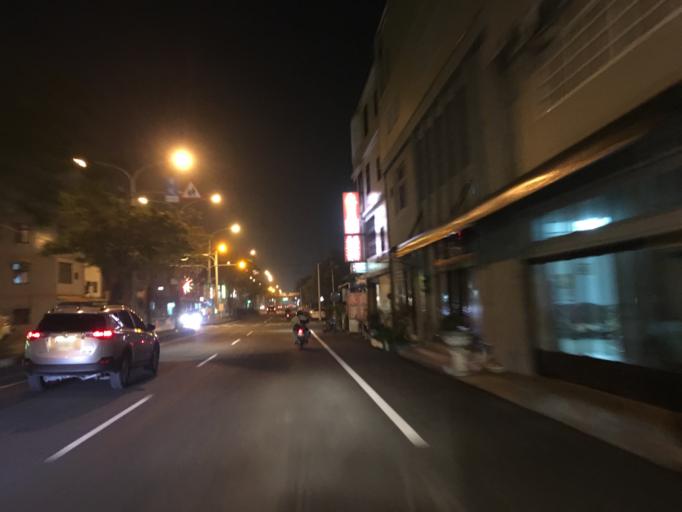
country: TW
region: Taiwan
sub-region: Miaoli
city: Miaoli
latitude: 24.6817
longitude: 120.8850
